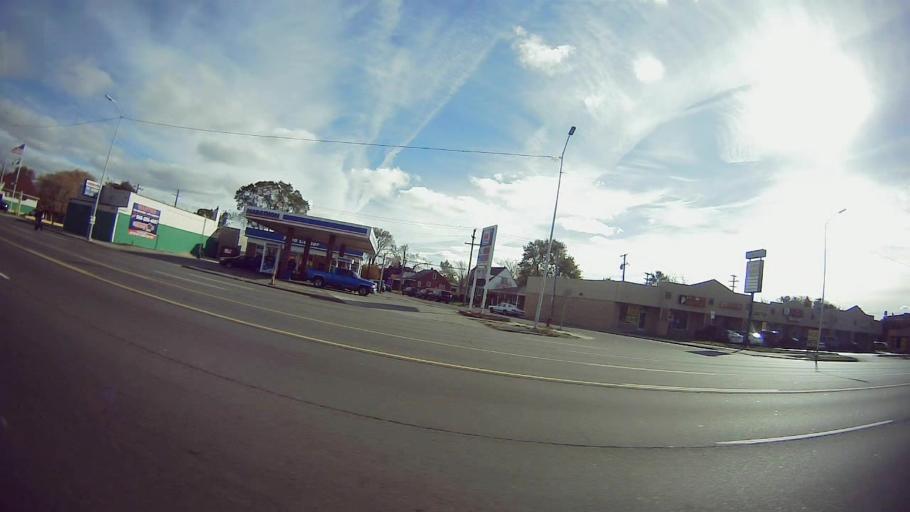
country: US
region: Michigan
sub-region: Macomb County
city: Eastpointe
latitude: 42.4456
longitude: -82.9712
